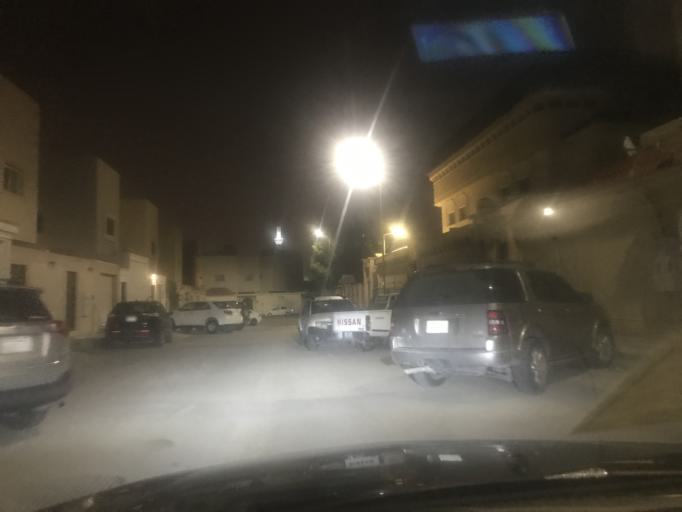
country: SA
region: Ar Riyad
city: Riyadh
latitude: 24.6926
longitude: 46.5987
